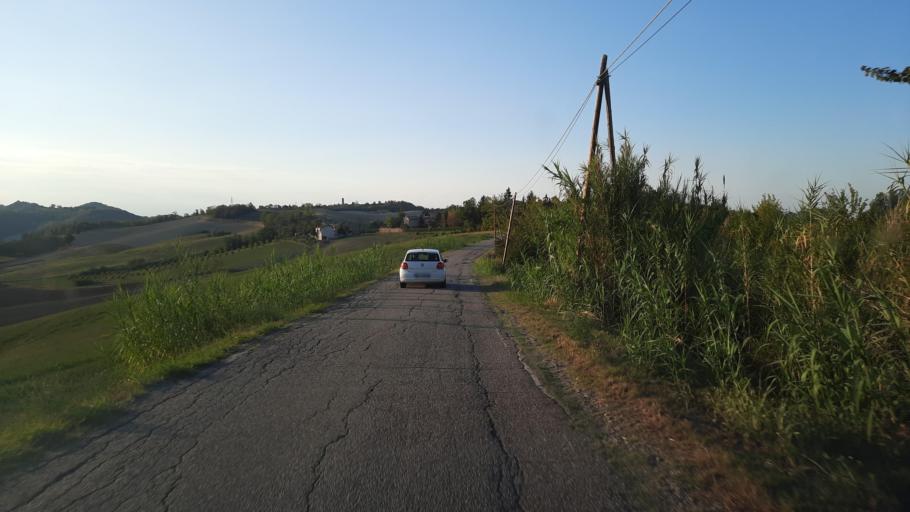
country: IT
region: Piedmont
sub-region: Provincia di Alessandria
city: Cereseto
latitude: 45.0716
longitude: 8.3288
